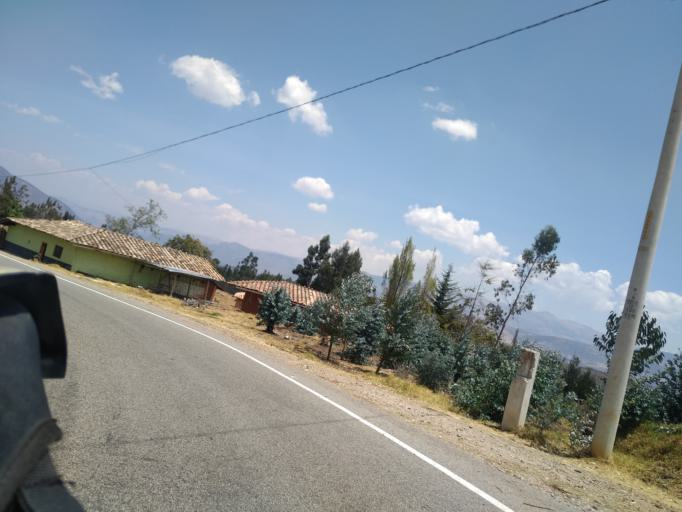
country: PE
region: Cajamarca
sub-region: San Marcos
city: San Marcos
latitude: -7.2882
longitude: -78.2064
